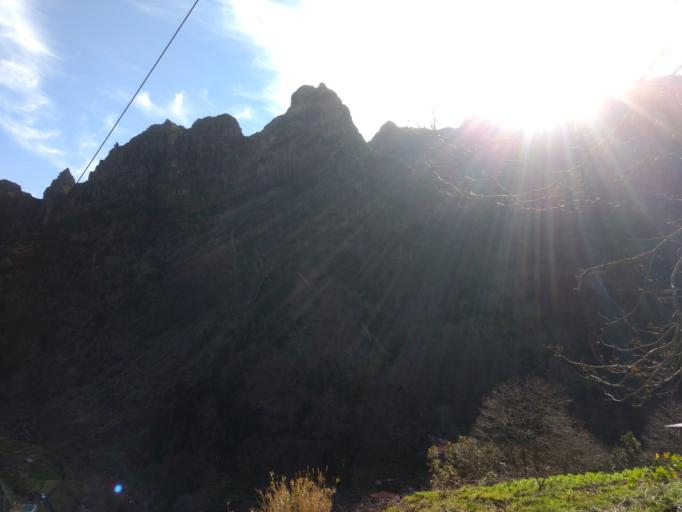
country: PT
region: Madeira
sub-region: Camara de Lobos
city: Curral das Freiras
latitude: 32.7459
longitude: -16.9657
